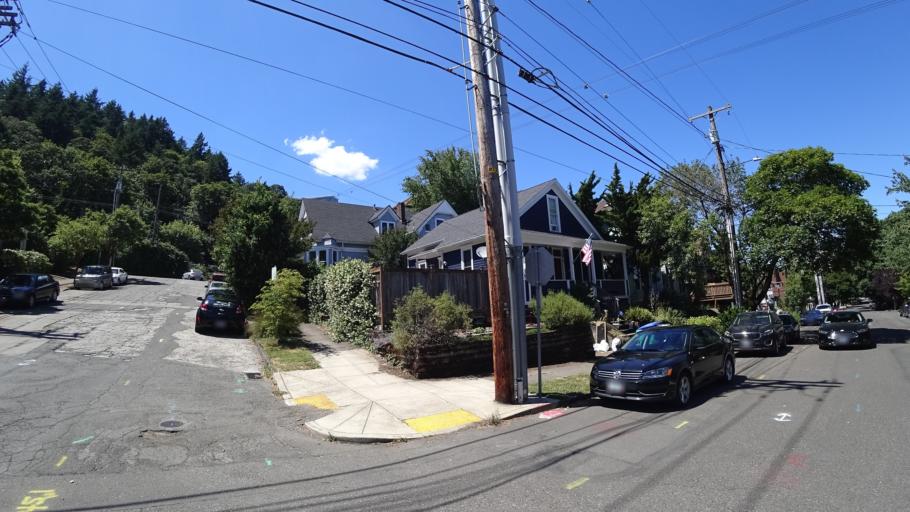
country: US
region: Oregon
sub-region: Multnomah County
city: Portland
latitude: 45.4987
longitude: -122.6789
